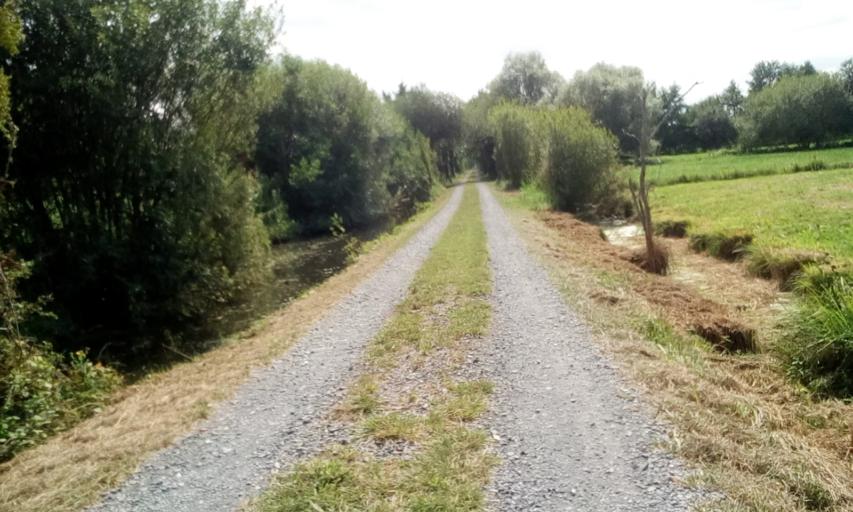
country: FR
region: Lower Normandy
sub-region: Departement du Calvados
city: Bavent
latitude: 49.2325
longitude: -0.1674
